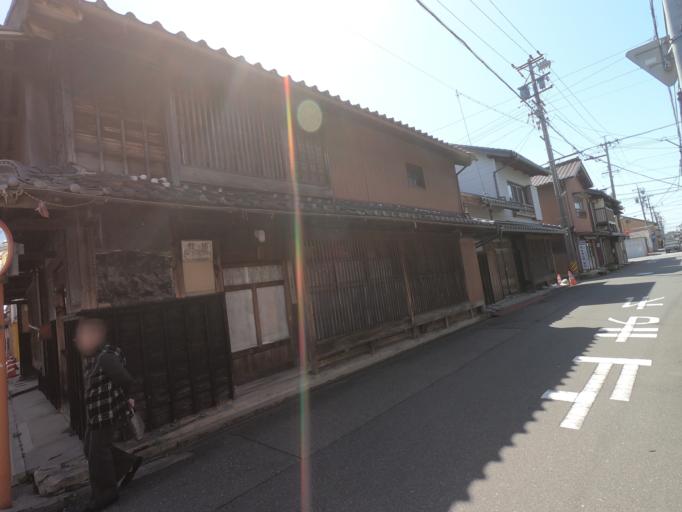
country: JP
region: Mie
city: Yokkaichi
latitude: 35.0080
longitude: 136.6627
